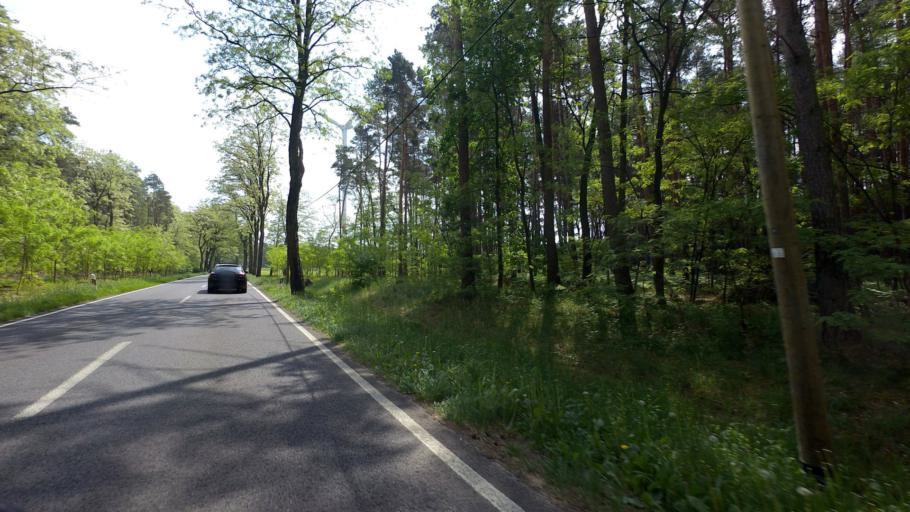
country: DE
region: Brandenburg
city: Neu Zauche
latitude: 51.9949
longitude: 14.1012
